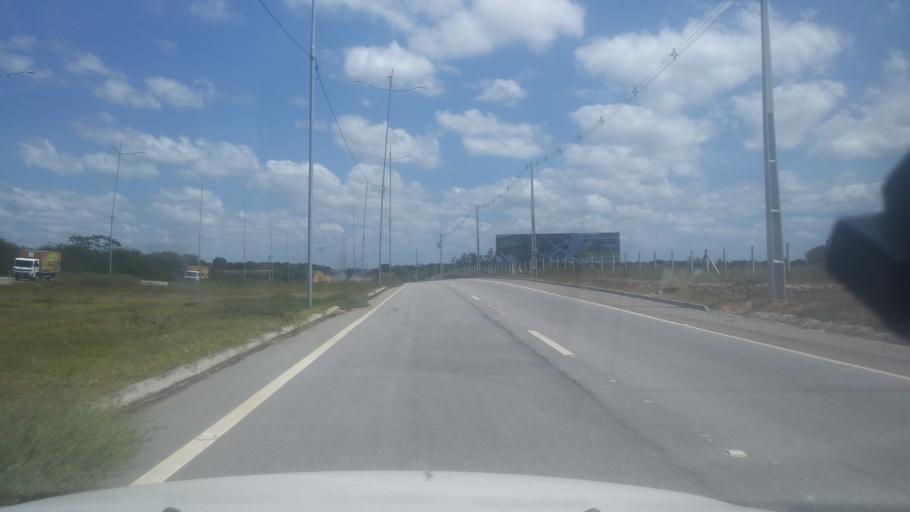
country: BR
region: Rio Grande do Norte
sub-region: Macaiba
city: Macaiba
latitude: -5.8400
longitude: -35.3758
